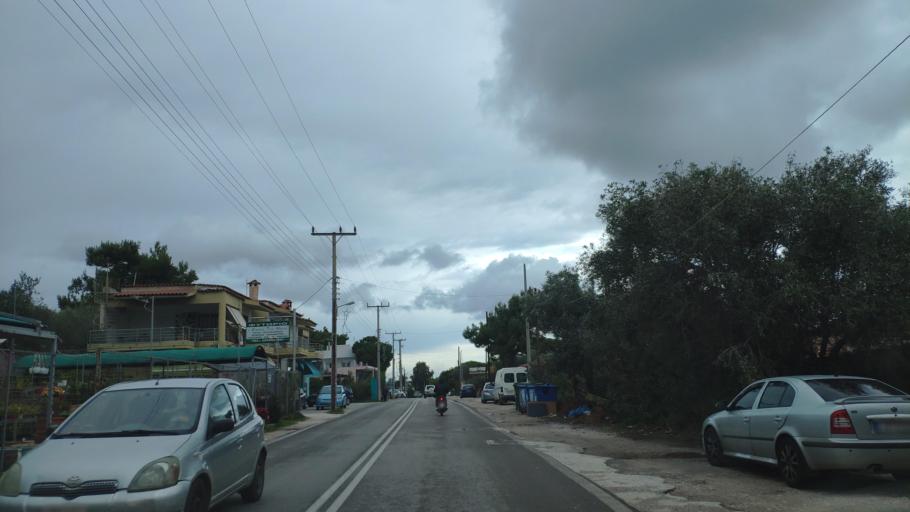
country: GR
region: Attica
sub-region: Nomarchia Anatolikis Attikis
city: Artemida
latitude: 37.9618
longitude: 24.0057
